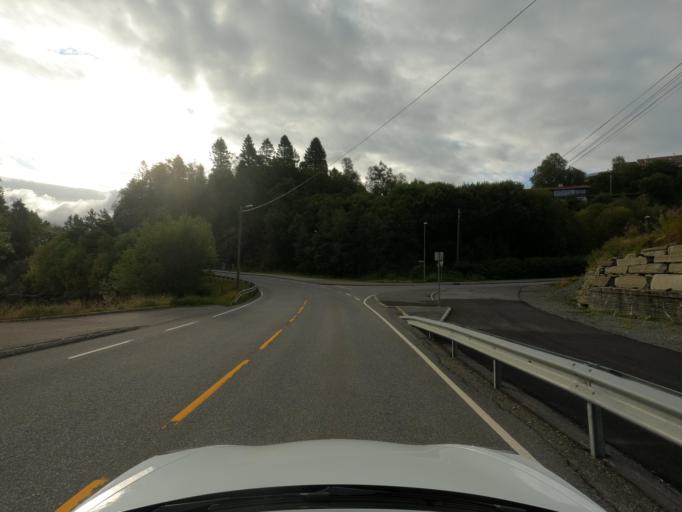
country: NO
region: Hordaland
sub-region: Bergen
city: Sandsli
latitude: 60.3099
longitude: 5.2961
